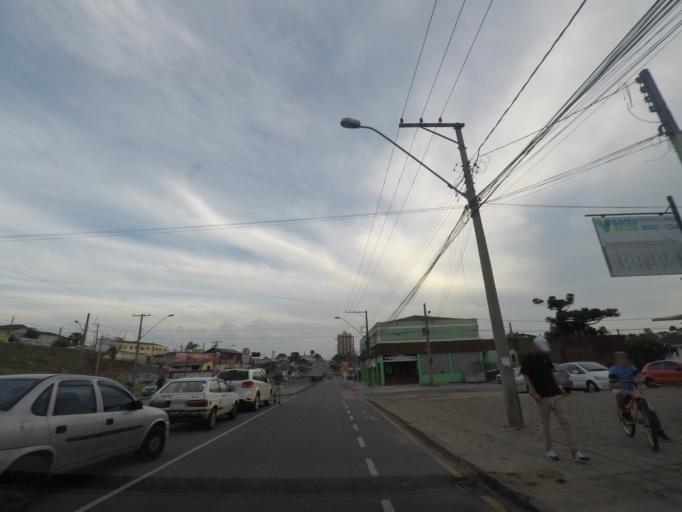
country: BR
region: Parana
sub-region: Curitiba
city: Curitiba
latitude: -25.3793
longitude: -49.2275
